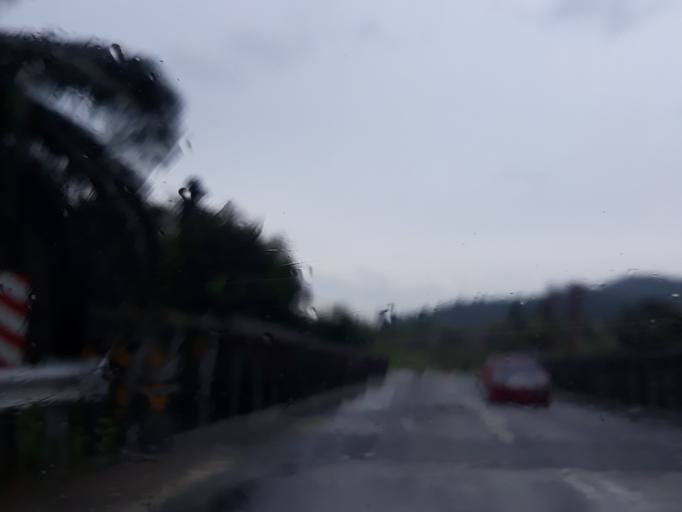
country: MY
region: Kedah
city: Kulim
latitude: 5.3470
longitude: 100.5859
